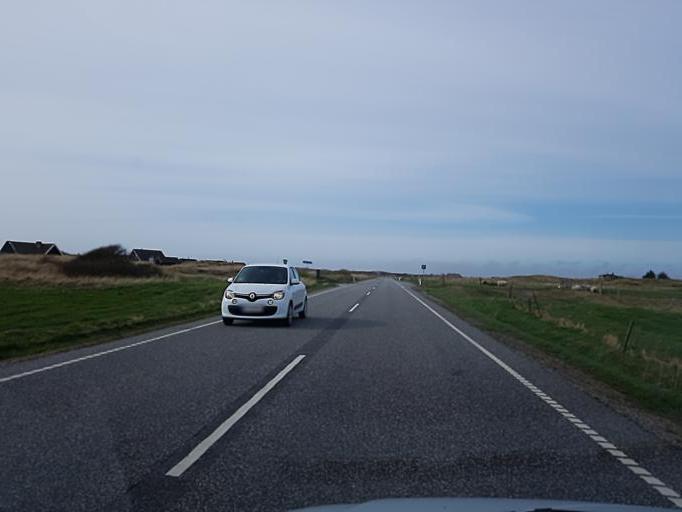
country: DK
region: Central Jutland
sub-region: Ringkobing-Skjern Kommune
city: Hvide Sande
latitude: 55.8865
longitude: 8.1753
